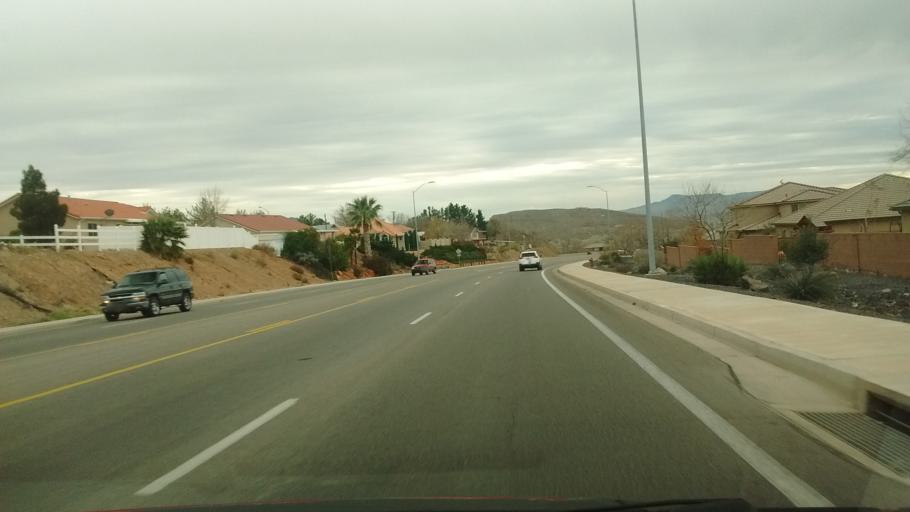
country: US
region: Utah
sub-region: Washington County
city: Washington
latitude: 37.1232
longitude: -113.5053
